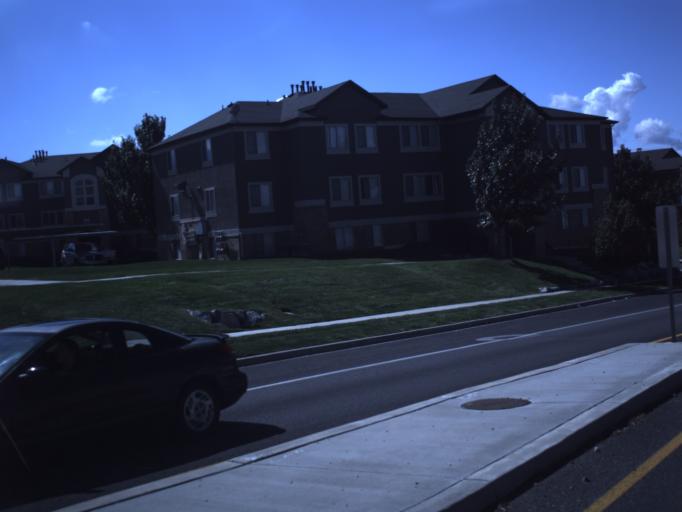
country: US
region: Utah
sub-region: Utah County
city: Spanish Fork
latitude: 40.1153
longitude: -111.6335
